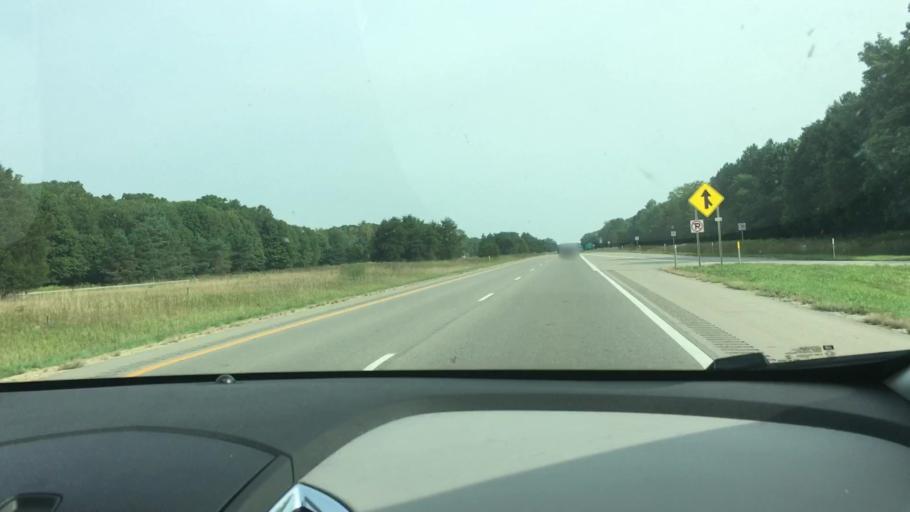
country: US
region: Michigan
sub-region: Kalamazoo County
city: Schoolcraft
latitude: 42.1738
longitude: -85.6449
